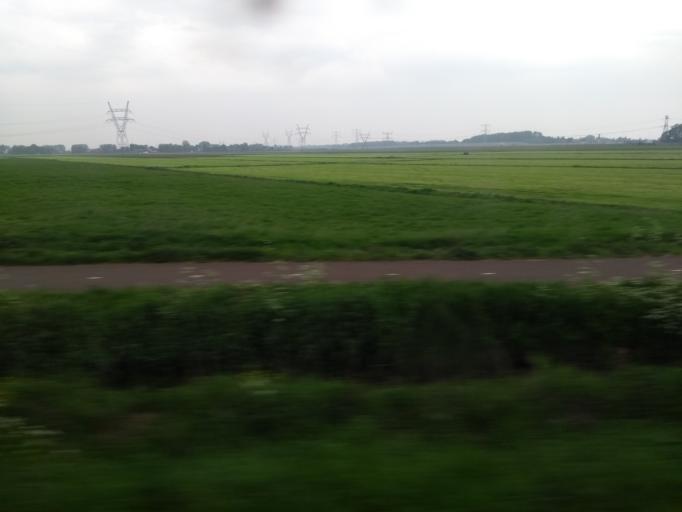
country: NL
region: North Holland
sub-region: Gemeente Weesp
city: Weesp
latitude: 52.3130
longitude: 5.0803
